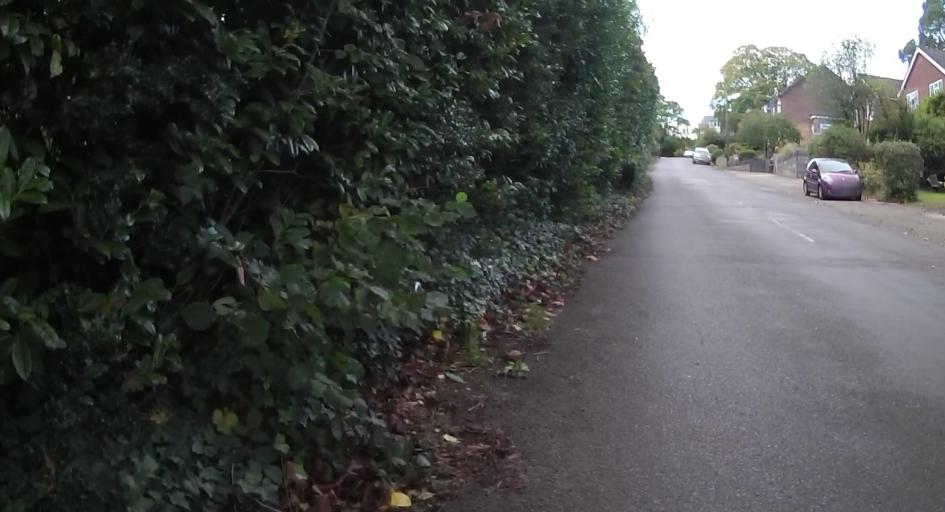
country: GB
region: England
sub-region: Surrey
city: Farnham
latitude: 51.1956
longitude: -0.8080
